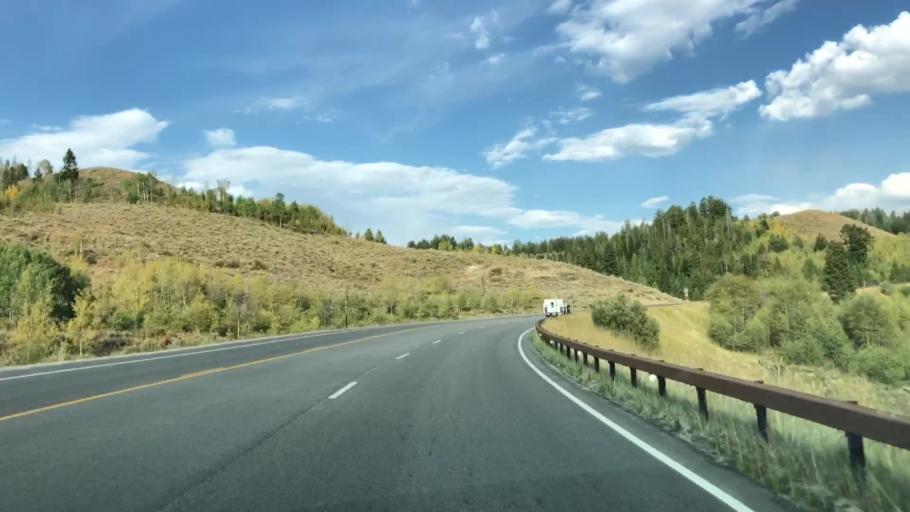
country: US
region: Wyoming
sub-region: Sublette County
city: Pinedale
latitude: 43.1389
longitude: -110.2200
